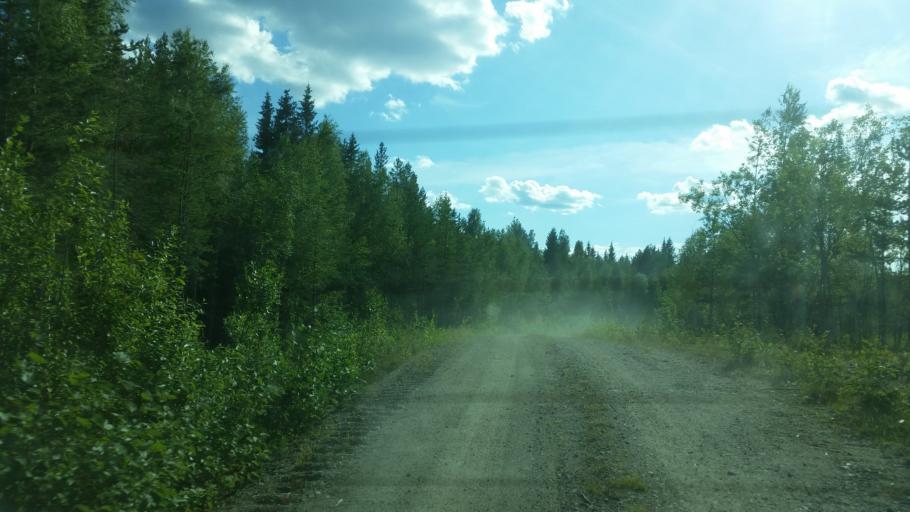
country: SE
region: Vaesternorrland
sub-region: Ange Kommun
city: Ange
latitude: 62.2721
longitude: 15.3937
